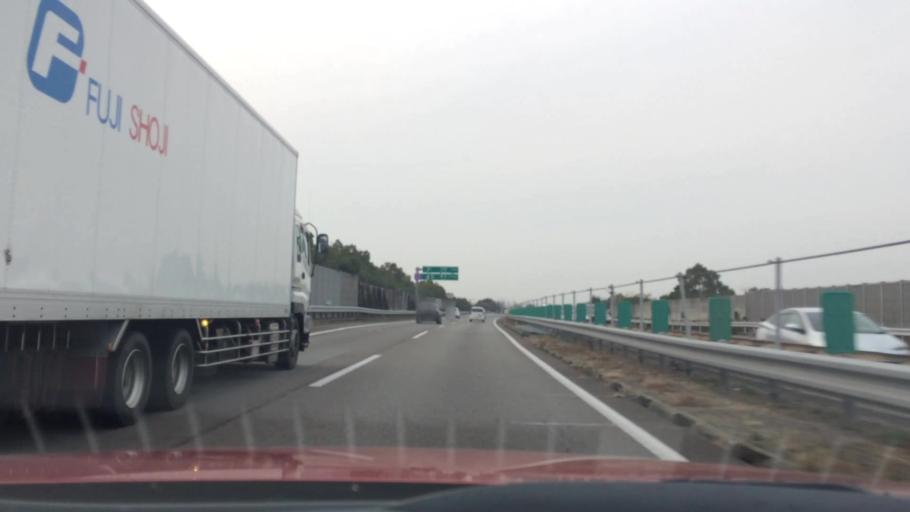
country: JP
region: Aichi
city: Sobue
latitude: 35.2867
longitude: 136.7467
